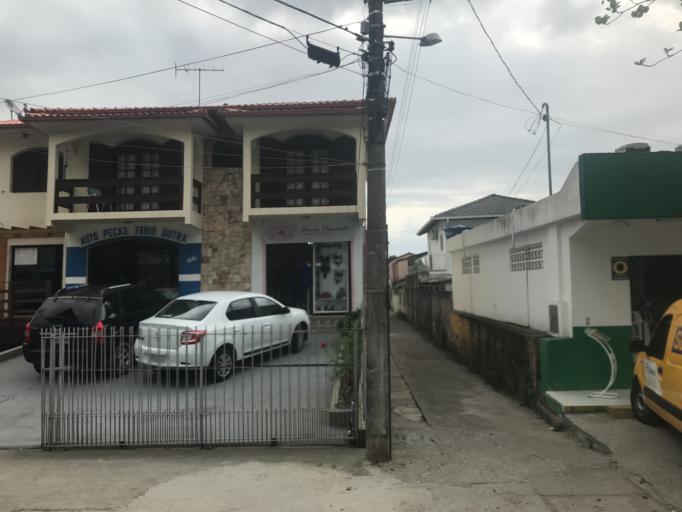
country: BR
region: Santa Catarina
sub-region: Florianopolis
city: Costeira do Pirajubae
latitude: -27.6328
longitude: -48.5236
